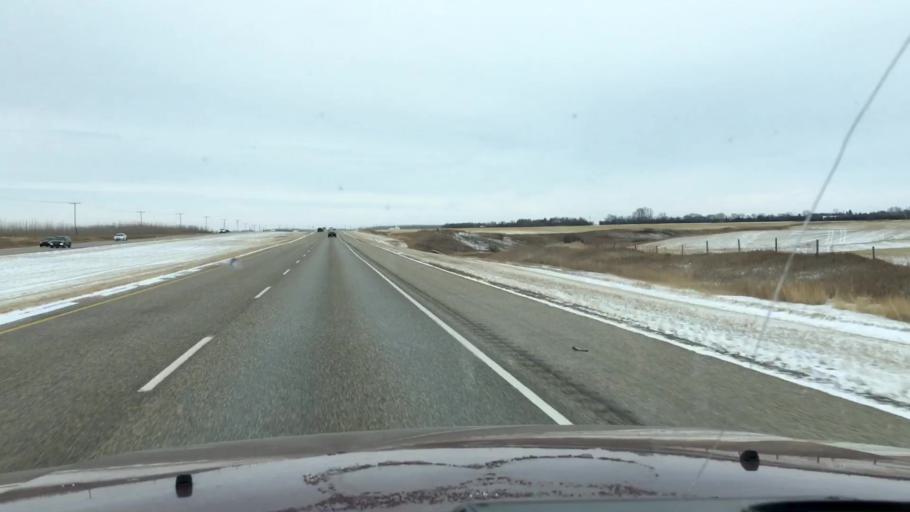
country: CA
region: Saskatchewan
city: Watrous
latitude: 51.0592
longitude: -105.8195
